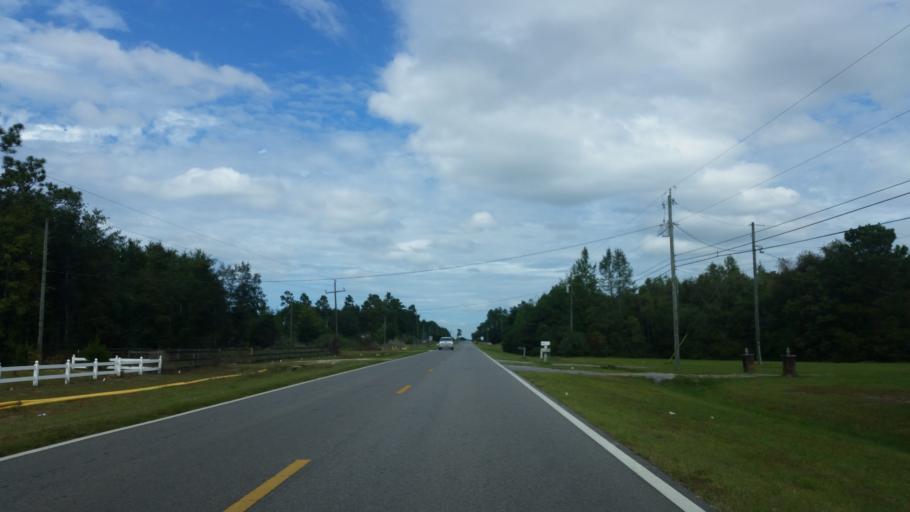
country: US
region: Florida
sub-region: Santa Rosa County
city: Point Baker
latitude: 30.6819
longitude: -86.9937
